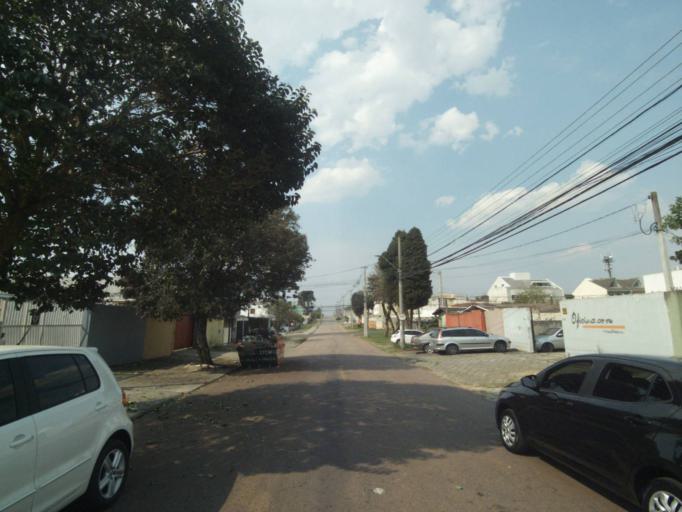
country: BR
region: Parana
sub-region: Curitiba
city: Curitiba
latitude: -25.4625
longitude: -49.2628
